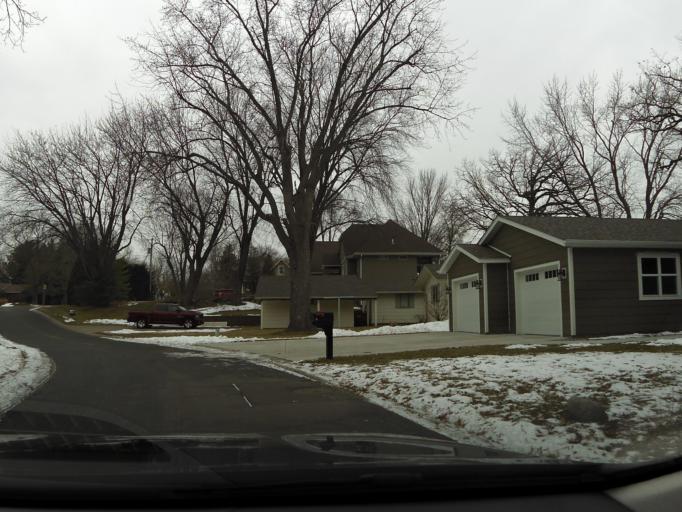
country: US
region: Minnesota
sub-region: Carver County
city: Waconia
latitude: 44.8590
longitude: -93.7938
